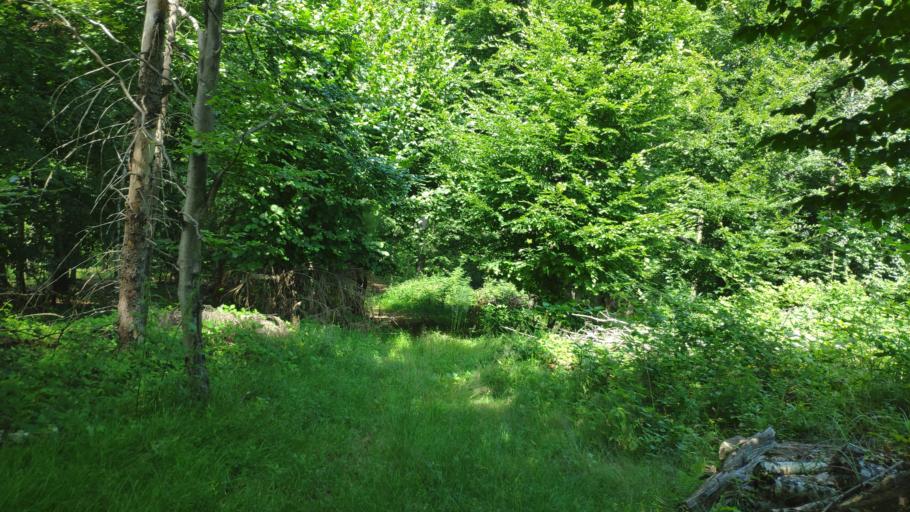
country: SK
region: Kosicky
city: Dobsina
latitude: 48.7064
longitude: 20.3836
